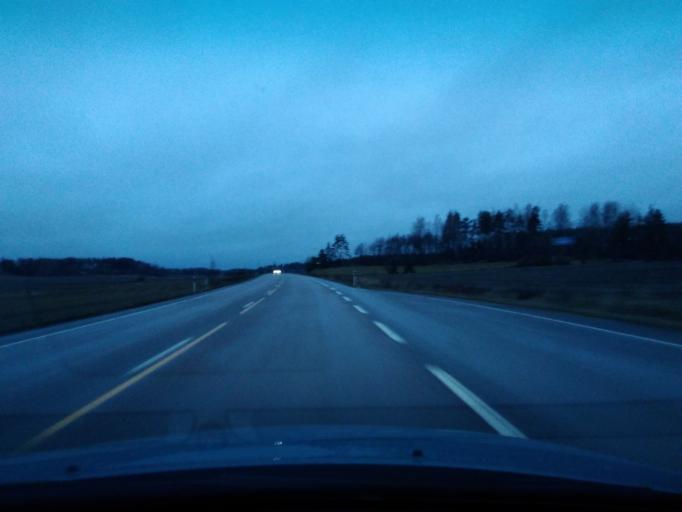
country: FI
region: Uusimaa
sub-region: Porvoo
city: Askola
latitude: 60.4763
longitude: 25.5678
